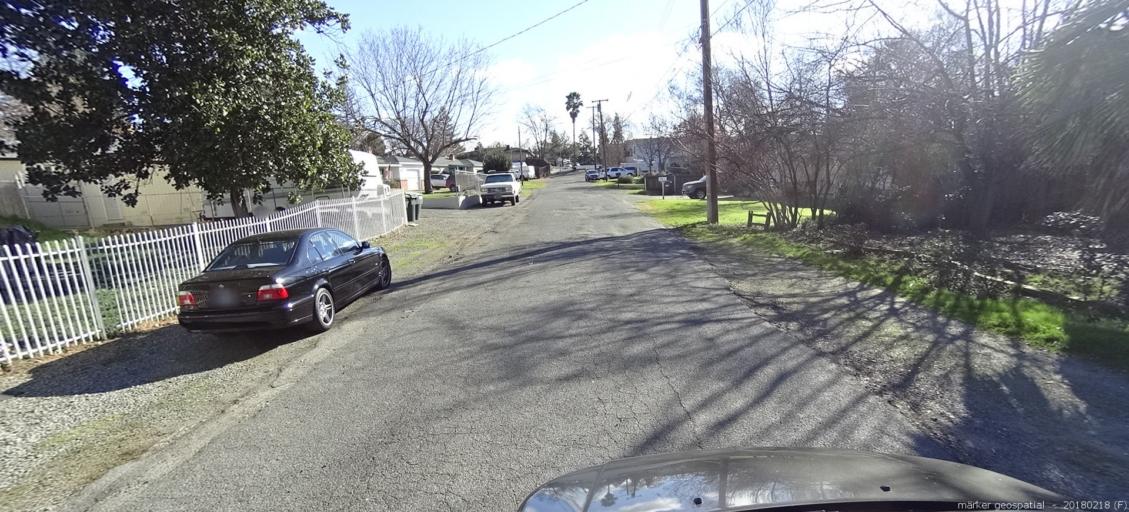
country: US
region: California
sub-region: Sacramento County
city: Orangevale
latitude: 38.6763
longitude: -121.2341
